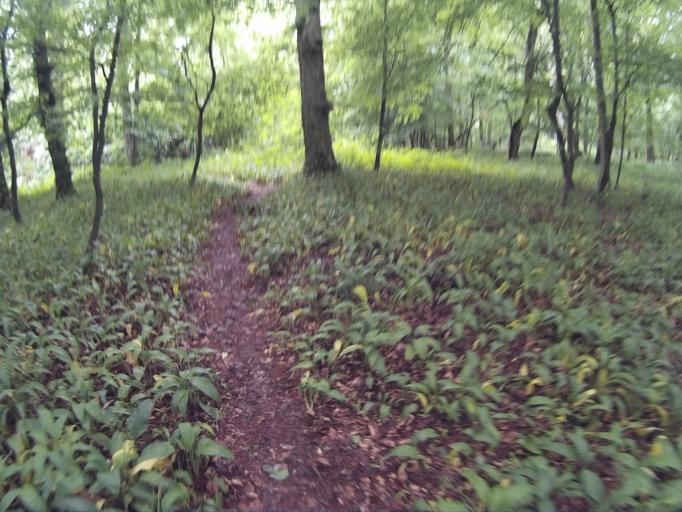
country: HU
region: Veszprem
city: Sumeg
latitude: 46.9036
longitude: 17.2571
